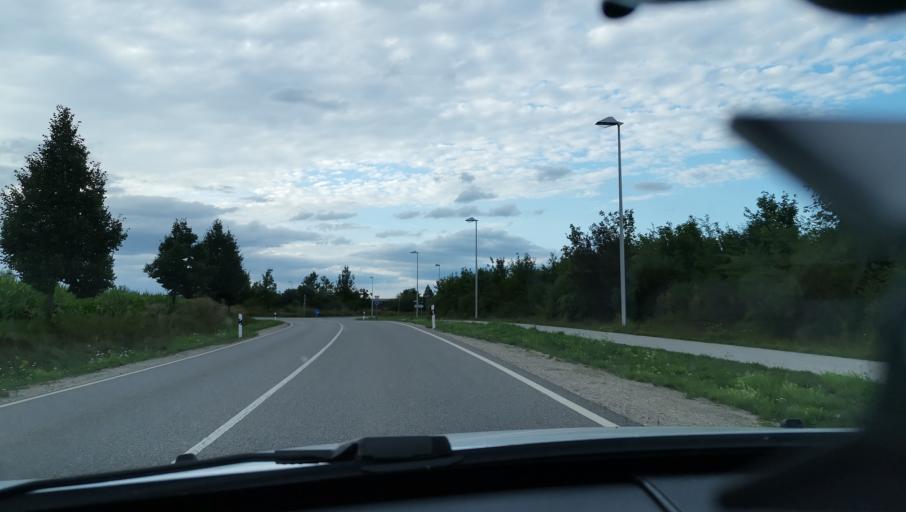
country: DE
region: Bavaria
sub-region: Regierungsbezirk Mittelfranken
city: Zirndorf
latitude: 49.4387
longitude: 10.9381
